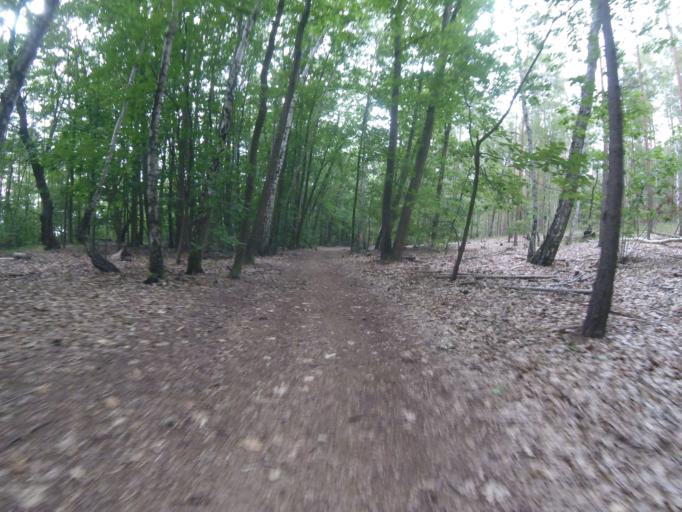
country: DE
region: Brandenburg
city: Bestensee
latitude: 52.2381
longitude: 13.6584
